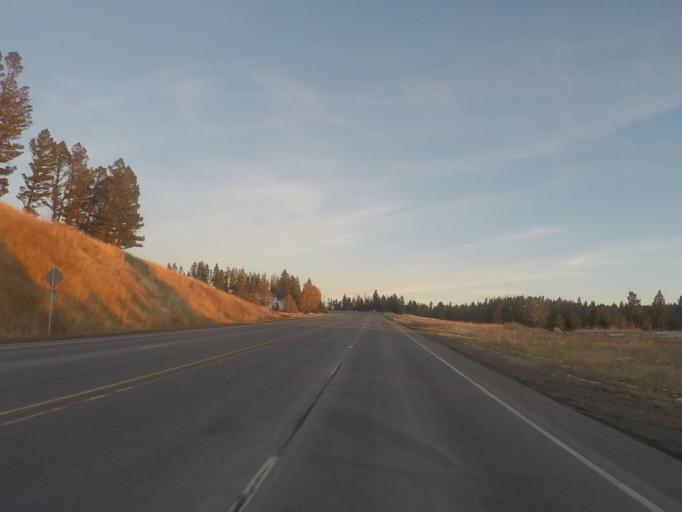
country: US
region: Montana
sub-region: Lewis and Clark County
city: Helena West Side
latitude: 46.5595
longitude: -112.3329
